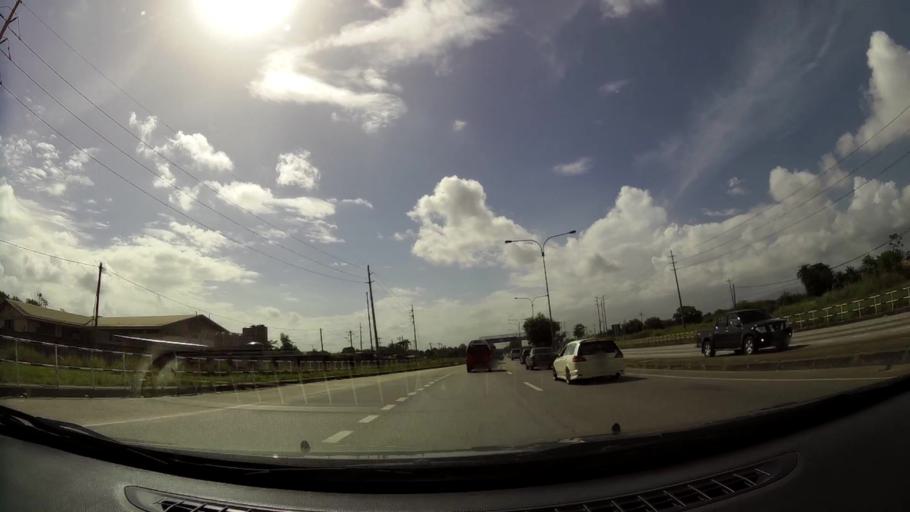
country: TT
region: Borough of Arima
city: Arima
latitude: 10.6076
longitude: -61.2706
